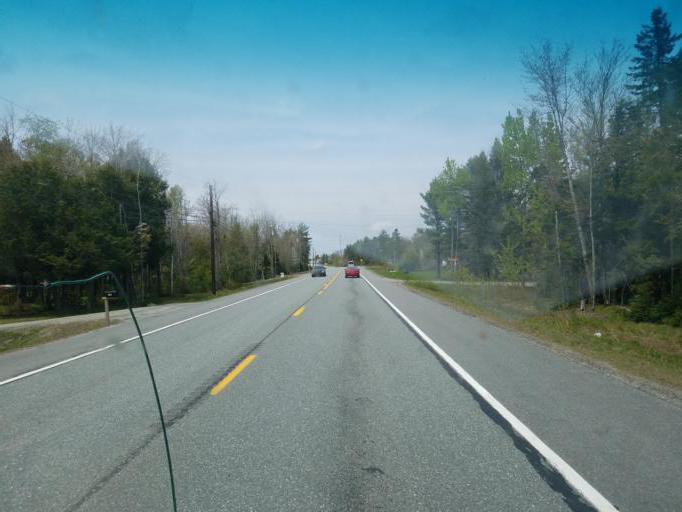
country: US
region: Maine
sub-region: Hancock County
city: Surry
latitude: 44.6102
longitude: -68.5203
